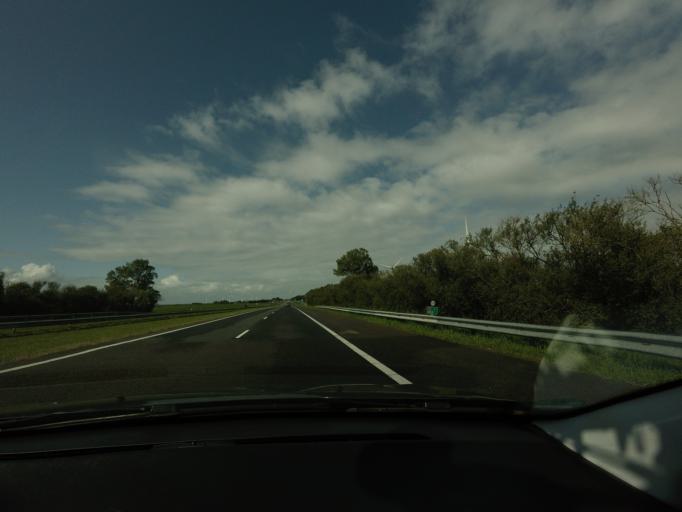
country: NL
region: Friesland
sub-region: Sudwest Fryslan
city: Makkum
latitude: 53.0892
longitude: 5.4416
